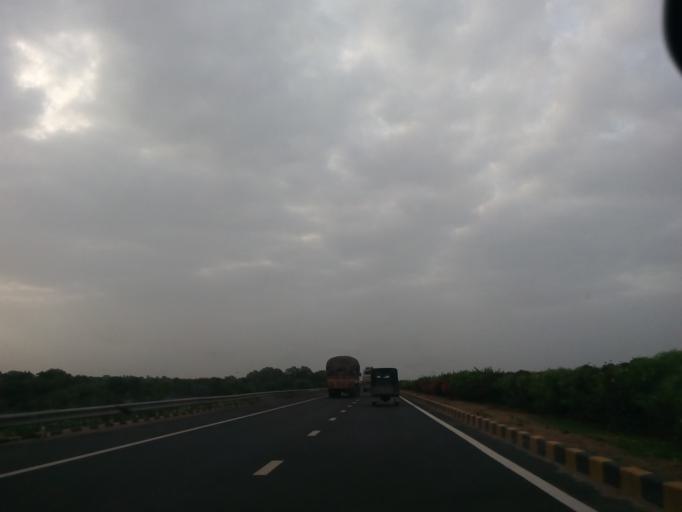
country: IN
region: Gujarat
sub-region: Kheda
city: Mahemdavad
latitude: 22.9316
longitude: 72.7307
